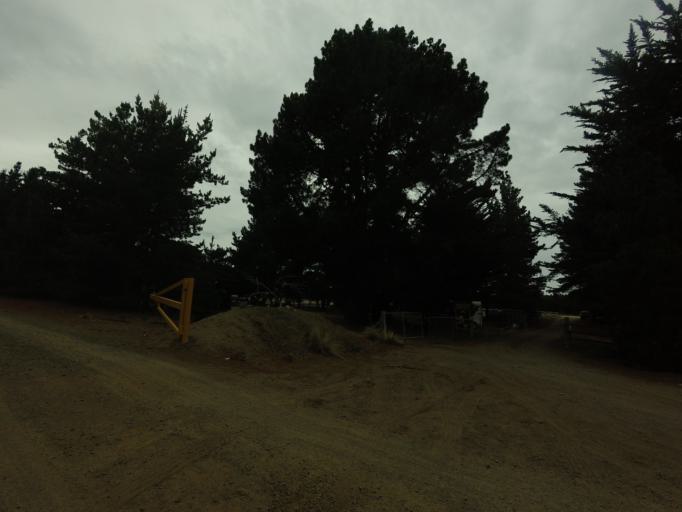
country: AU
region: Tasmania
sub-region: Clarence
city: Seven Mile Beach
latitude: -42.8337
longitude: 147.5385
